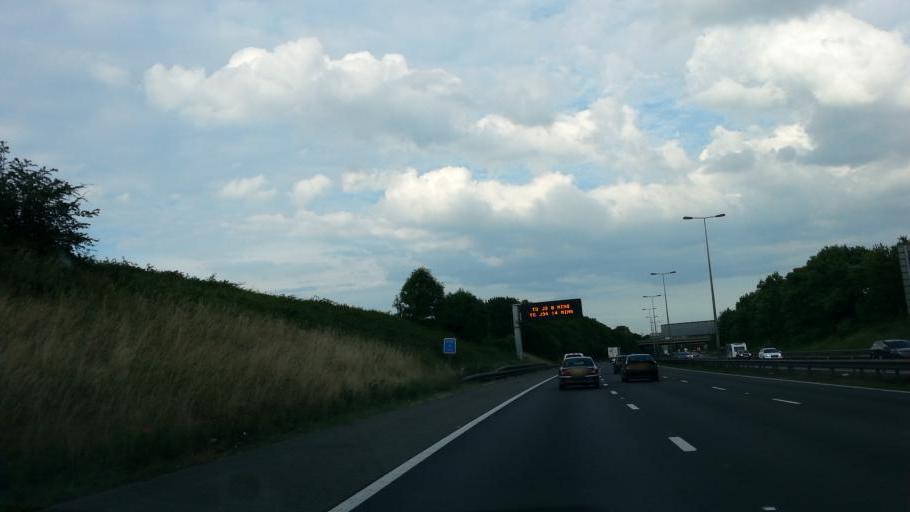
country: GB
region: England
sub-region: Worcestershire
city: Bromsgrove
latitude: 52.3561
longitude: -2.0525
